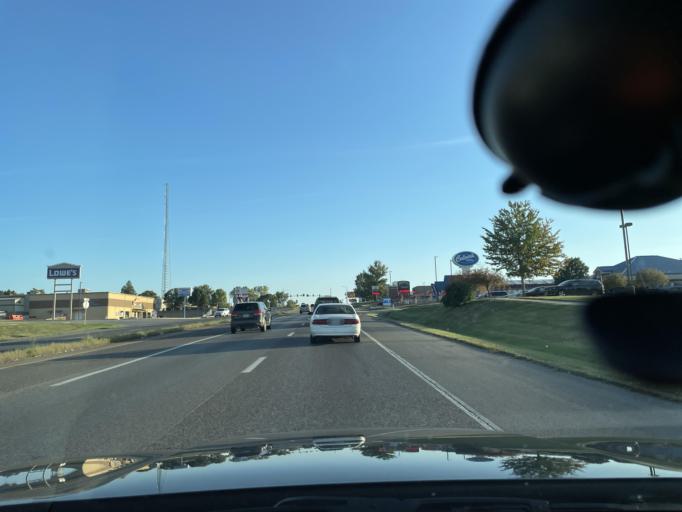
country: US
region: Missouri
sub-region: Andrew County
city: Country Club Village
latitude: 39.8056
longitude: -94.8153
